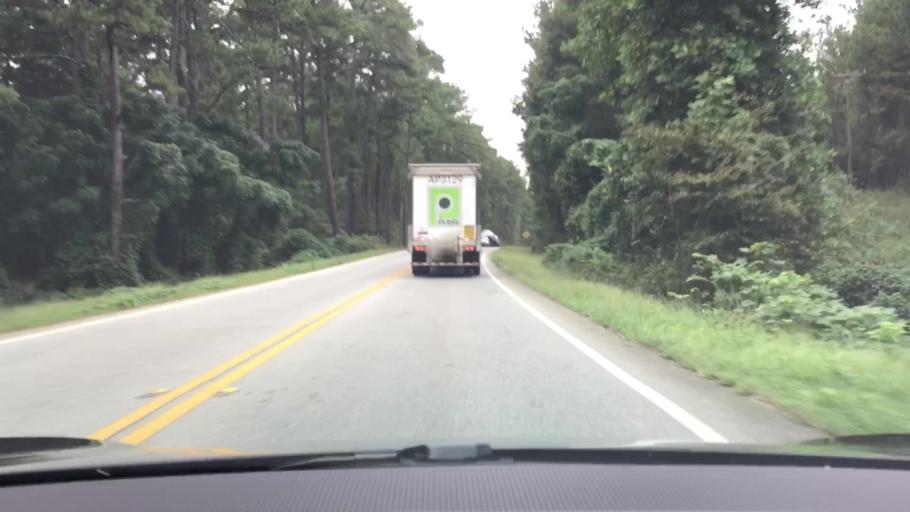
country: US
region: Georgia
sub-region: Greene County
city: Greensboro
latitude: 33.6797
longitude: -83.2708
